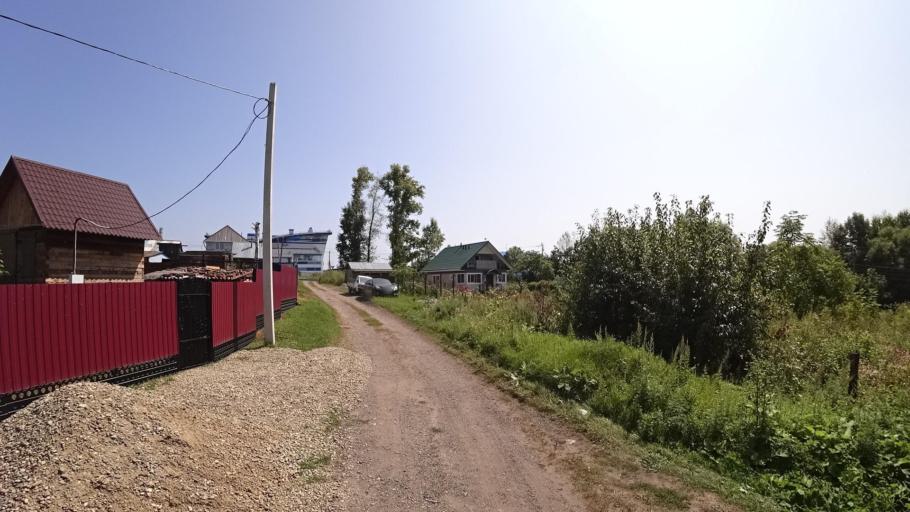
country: RU
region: Khabarovsk Krai
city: Khor
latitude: 47.9617
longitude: 135.1147
